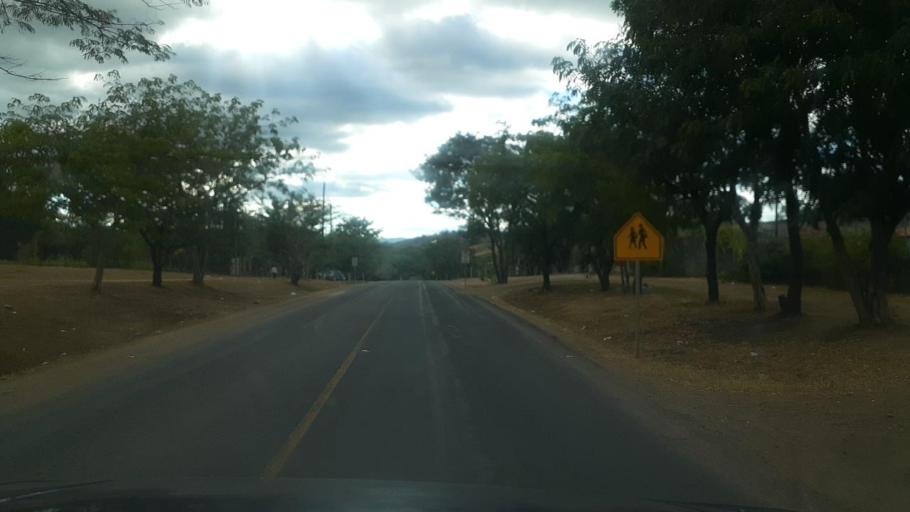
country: NI
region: Madriz
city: Somoto
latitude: 13.4773
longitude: -86.5917
